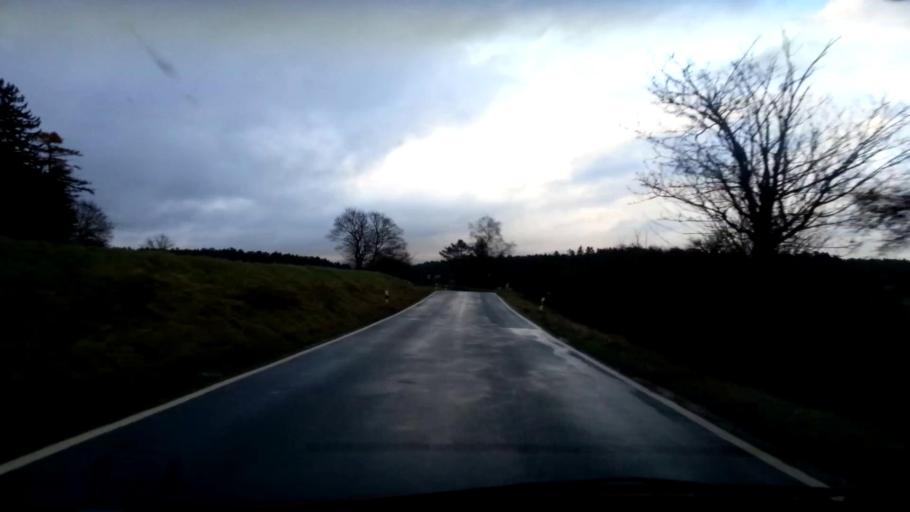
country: DE
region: Bavaria
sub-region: Upper Franconia
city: Poxdorf
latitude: 49.9232
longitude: 11.1293
